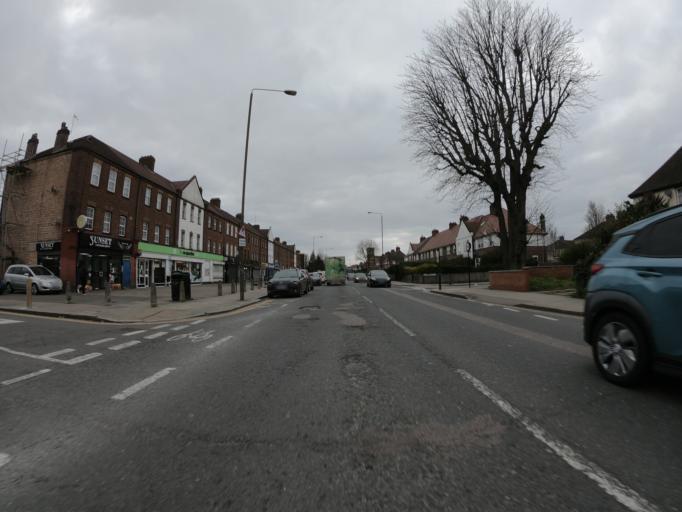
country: GB
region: England
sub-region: Greater London
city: Blackheath
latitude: 51.4746
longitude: 0.0356
